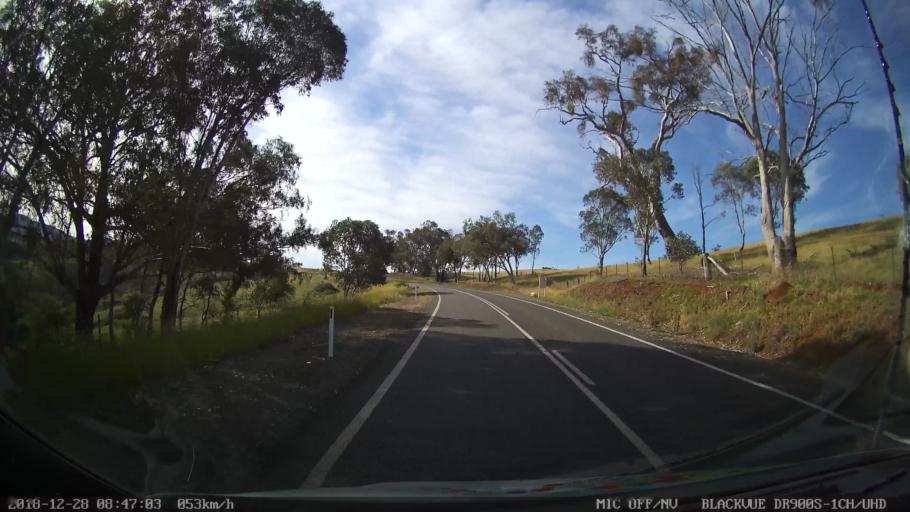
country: AU
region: New South Wales
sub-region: Upper Lachlan Shire
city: Crookwell
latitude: -34.0246
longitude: 149.3333
